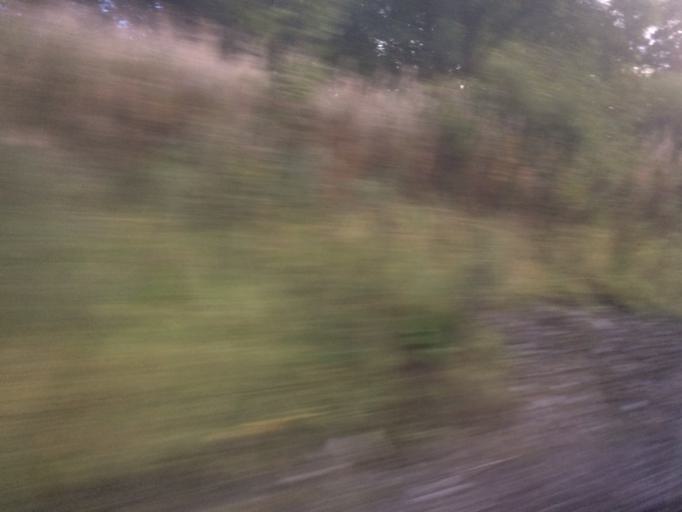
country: GB
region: Scotland
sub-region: North Lanarkshire
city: Cumbernauld
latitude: 55.9668
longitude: -4.0211
